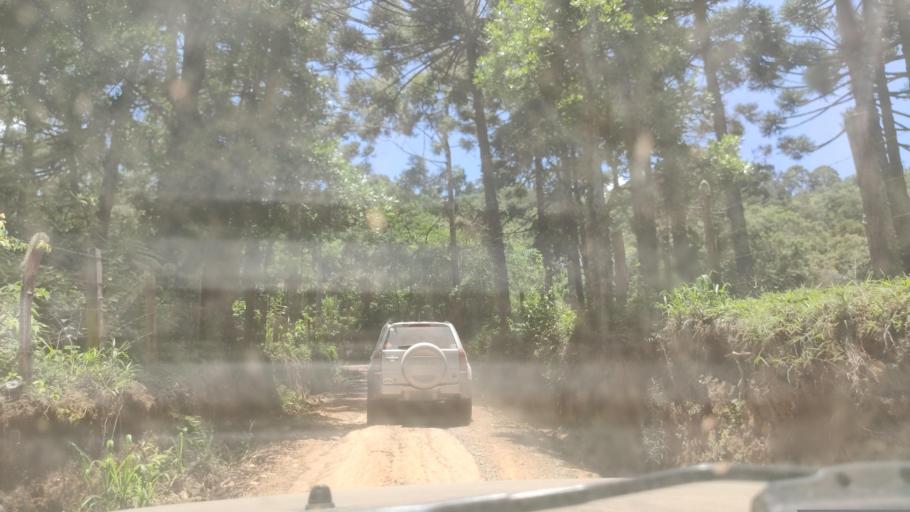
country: BR
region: Minas Gerais
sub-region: Cambui
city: Cambui
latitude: -22.6764
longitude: -45.9687
